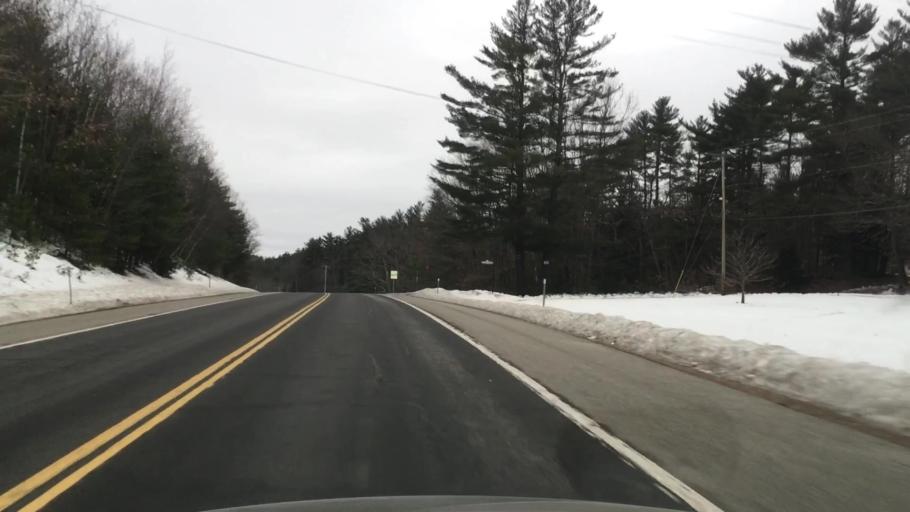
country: US
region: New Hampshire
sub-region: Merrimack County
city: Sutton
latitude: 43.2512
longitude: -71.9259
